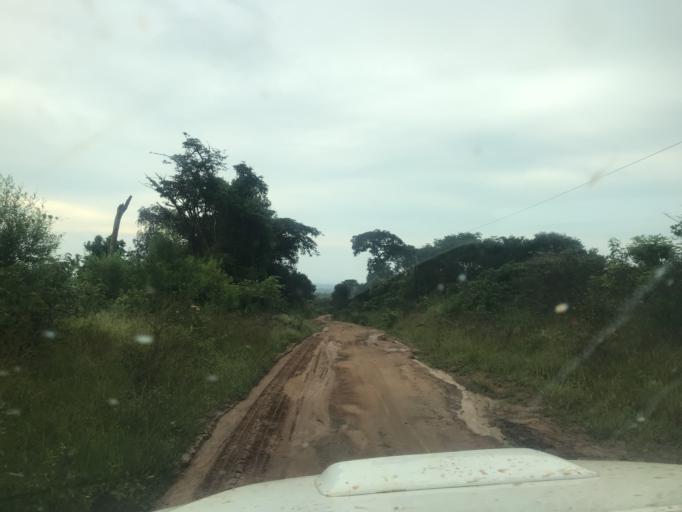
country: TZ
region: Mtwara
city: Newala Kisimani
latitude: -11.4041
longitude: 39.3856
